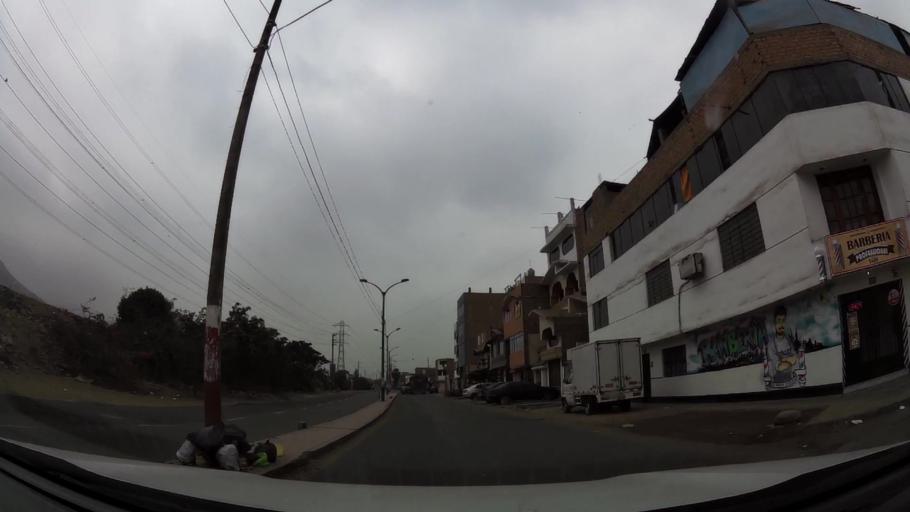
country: PE
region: Lima
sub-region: Lima
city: Independencia
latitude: -11.9412
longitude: -77.0868
